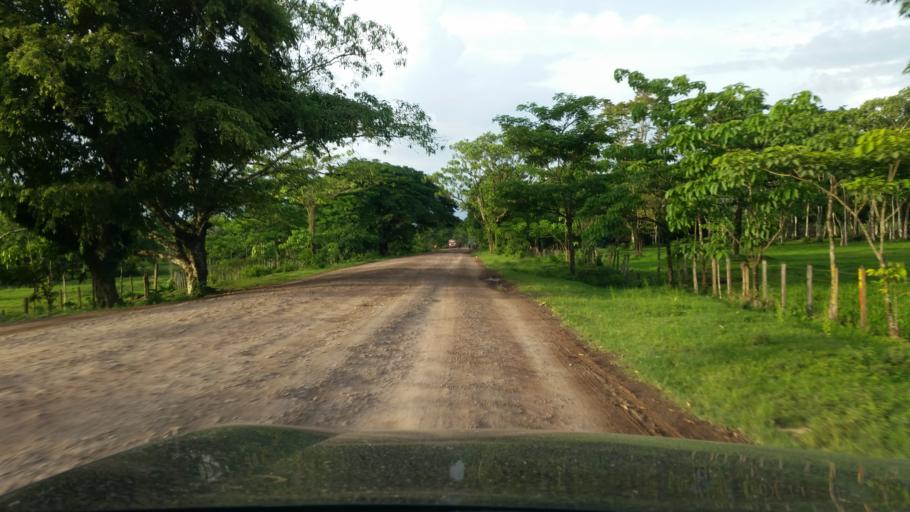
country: NI
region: Atlantico Norte (RAAN)
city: Siuna
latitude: 13.3237
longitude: -84.8972
